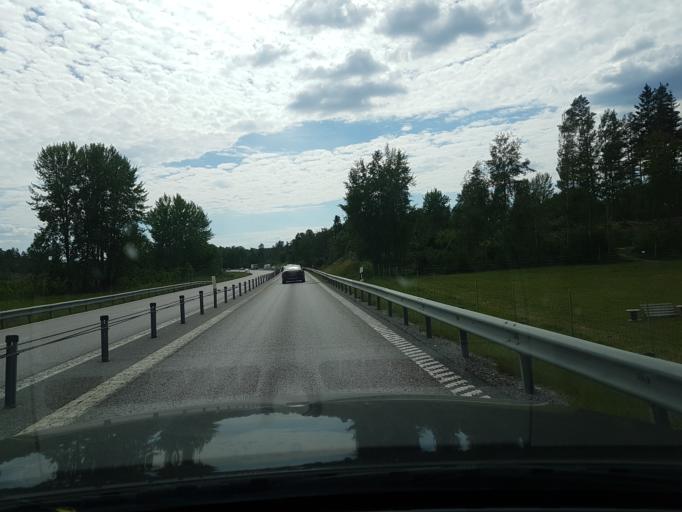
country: SE
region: Stockholm
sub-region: Osterakers Kommun
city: Akersberga
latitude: 59.5332
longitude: 18.1964
